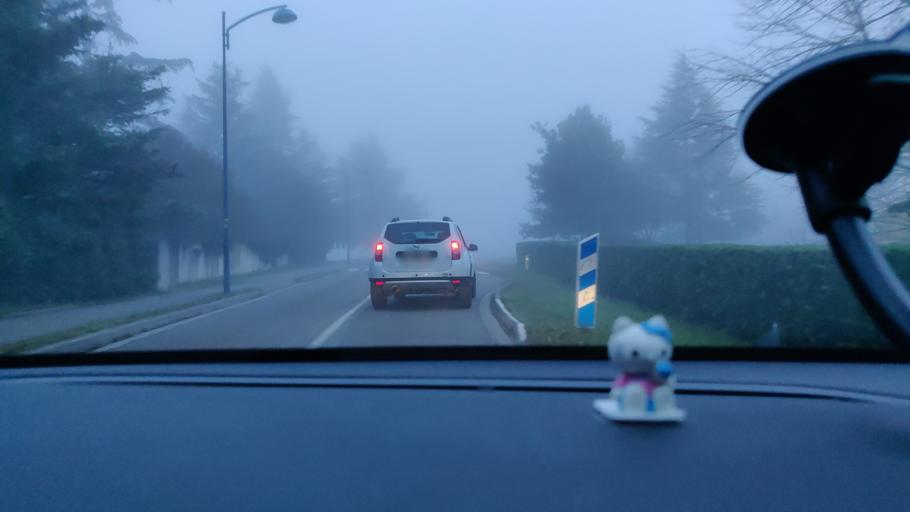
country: FR
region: Midi-Pyrenees
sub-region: Departement de la Haute-Garonne
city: Vieille-Toulouse
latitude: 43.5165
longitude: 1.4625
